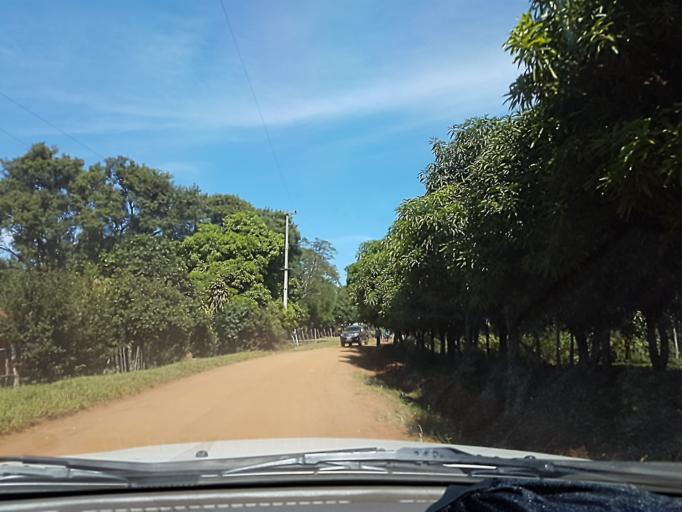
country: PY
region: Cordillera
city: Arroyos y Esteros
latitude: -24.9930
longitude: -57.2139
